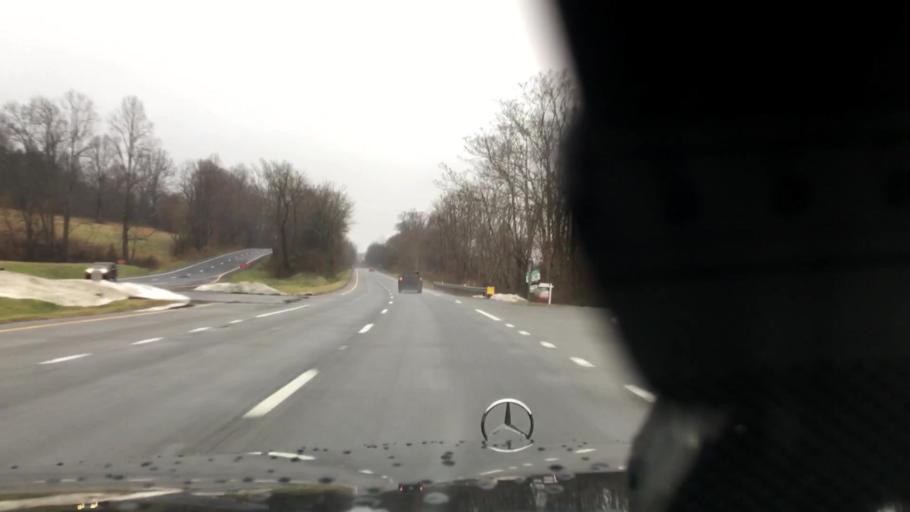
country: US
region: Virginia
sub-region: Nelson County
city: Nellysford
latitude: 37.8826
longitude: -78.7135
